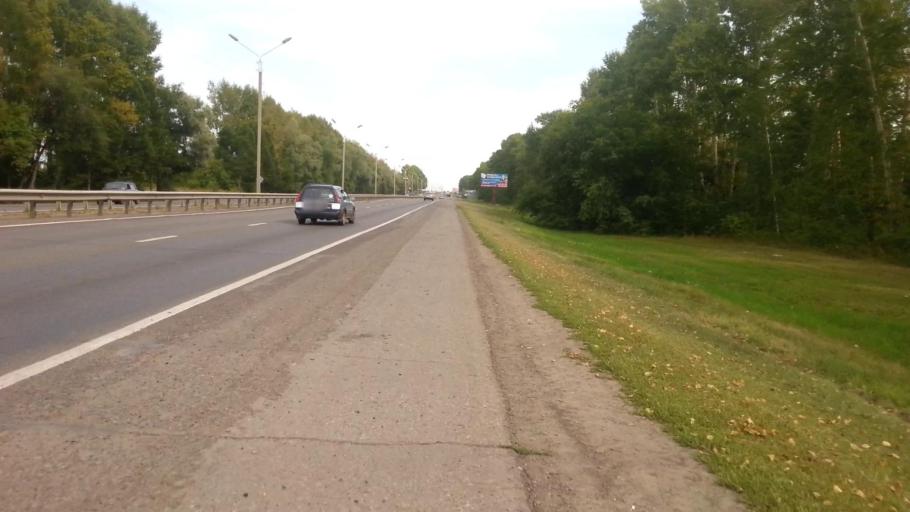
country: RU
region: Altai Krai
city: Vlasikha
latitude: 53.3524
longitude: 83.5715
